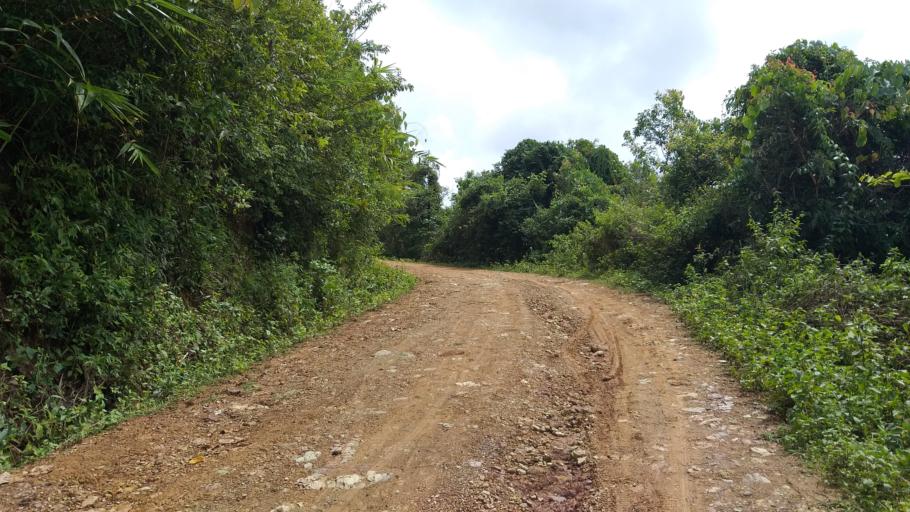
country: LA
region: Phongsali
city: Khoa
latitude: 21.3937
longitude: 102.6484
